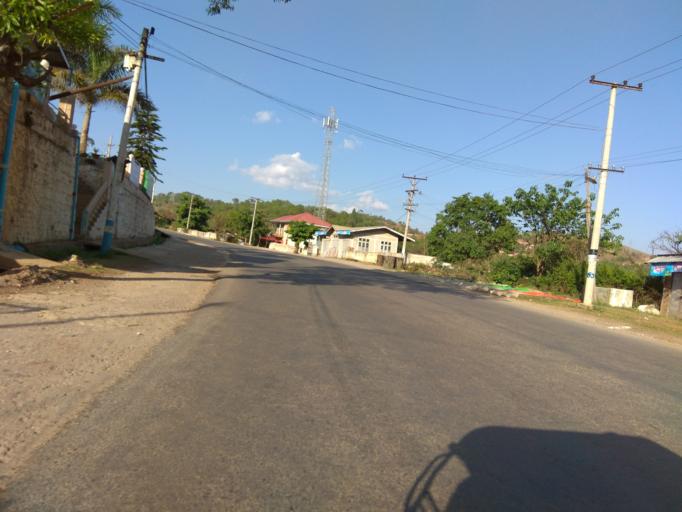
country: MM
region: Shan
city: Taunggyi
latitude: 20.6352
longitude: 96.5869
